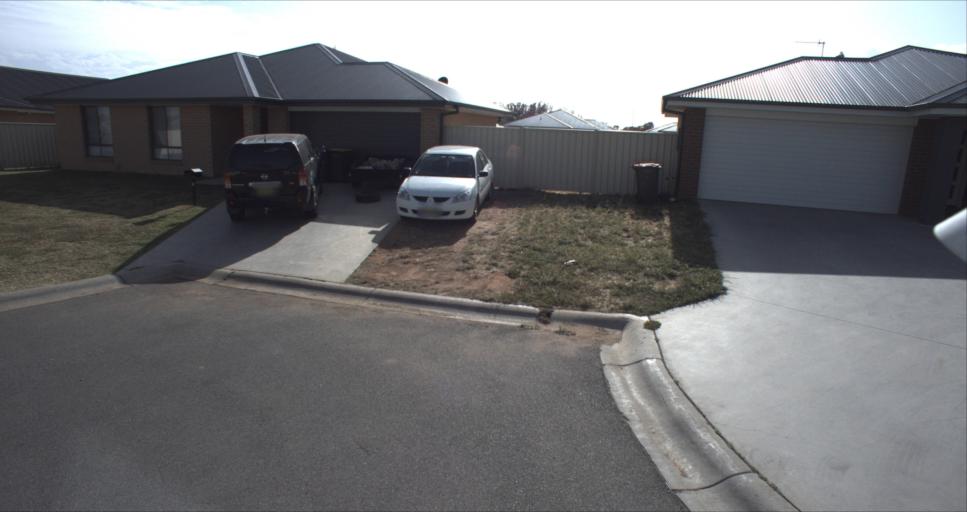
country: AU
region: New South Wales
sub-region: Leeton
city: Leeton
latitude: -34.5698
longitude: 146.3993
